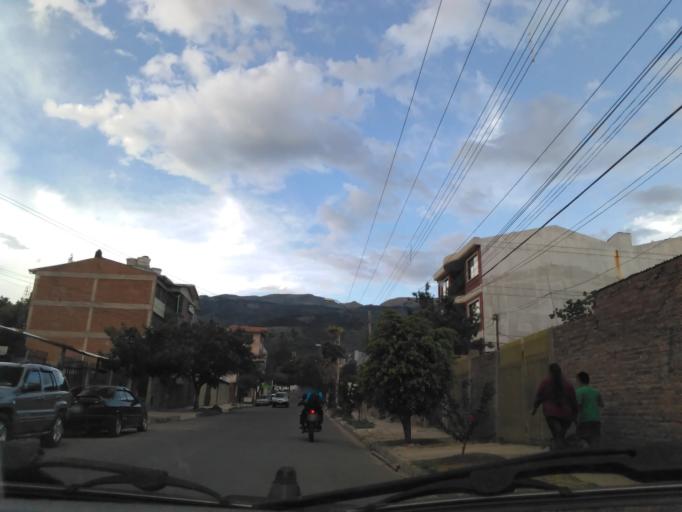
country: BO
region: Cochabamba
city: Cochabamba
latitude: -17.3720
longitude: -66.1536
